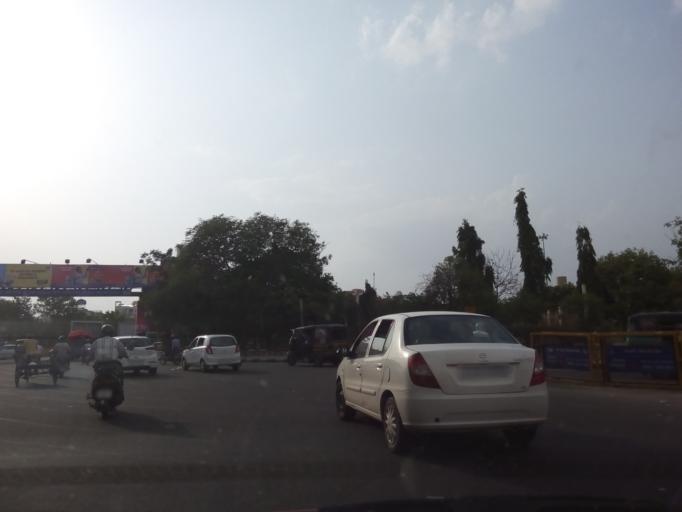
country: IN
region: Rajasthan
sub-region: Jaipur
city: Jaipur
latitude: 26.9254
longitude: 75.7930
